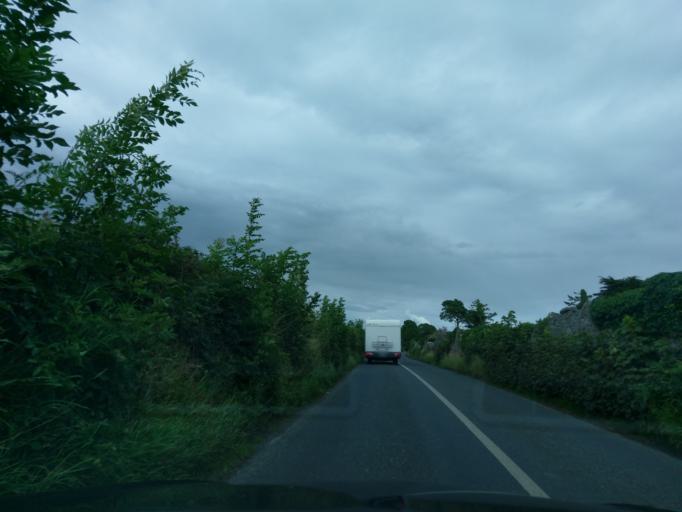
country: IE
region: Connaught
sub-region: County Galway
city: Gort
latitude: 53.1612
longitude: -8.7979
